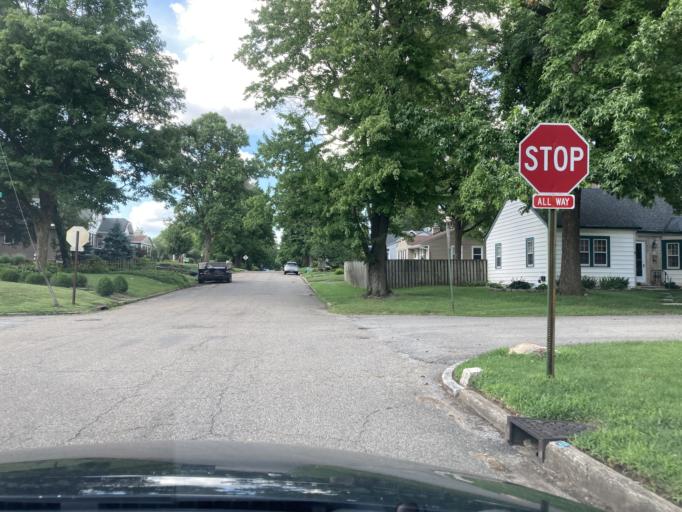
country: US
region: Indiana
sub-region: Marion County
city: Broad Ripple
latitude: 39.8638
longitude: -86.1340
